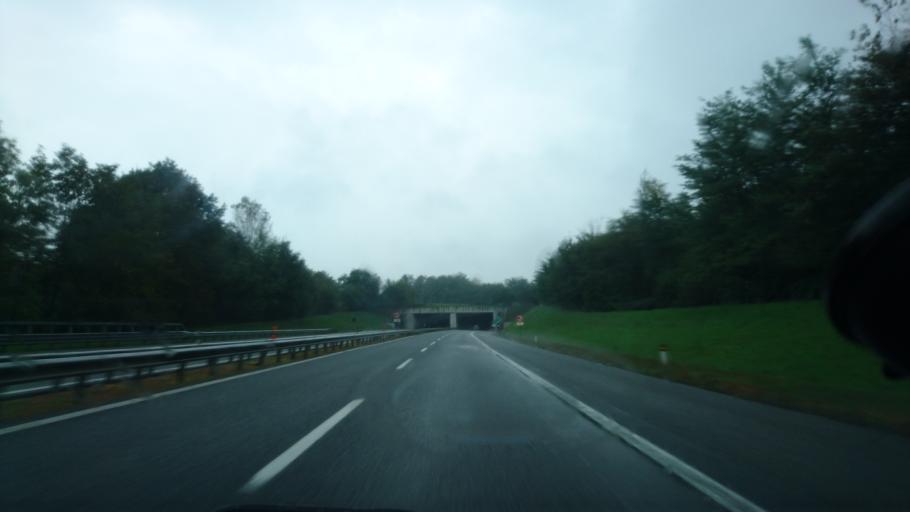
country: IT
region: Piedmont
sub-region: Provincia di Novara
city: Bogogno
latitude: 45.6723
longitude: 8.5266
